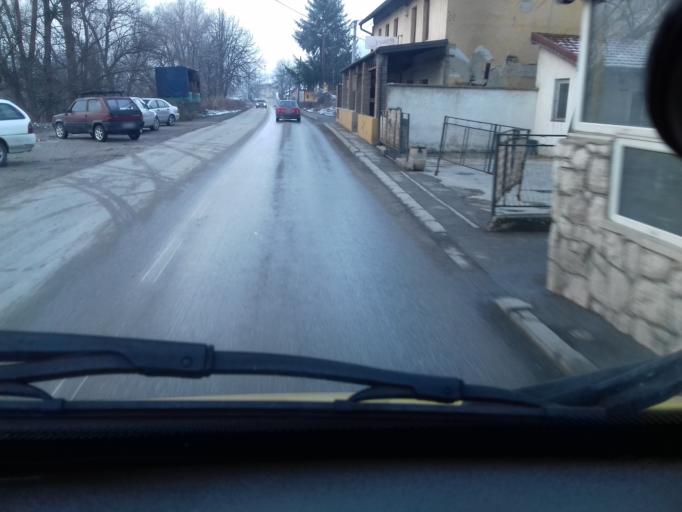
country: BA
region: Federation of Bosnia and Herzegovina
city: Visoko
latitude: 43.9940
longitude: 18.1841
